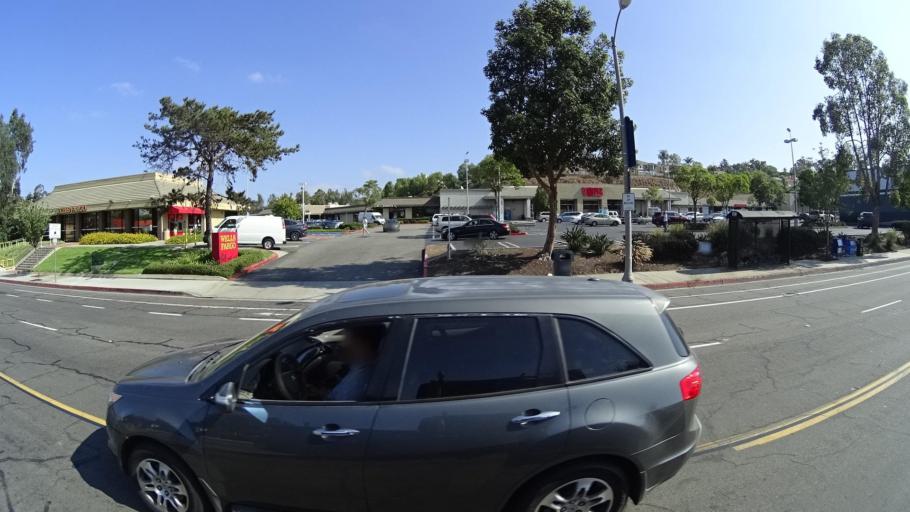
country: US
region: California
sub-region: San Diego County
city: Vista
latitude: 33.1935
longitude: -117.2335
